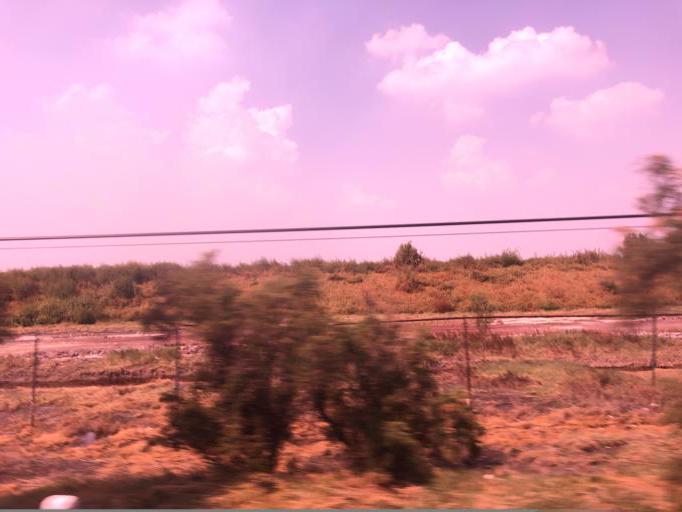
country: MX
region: Mexico
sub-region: Ciudad Nezahualcoyotl
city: Colonia Gustavo Baz Prada
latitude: 19.4641
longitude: -99.0195
